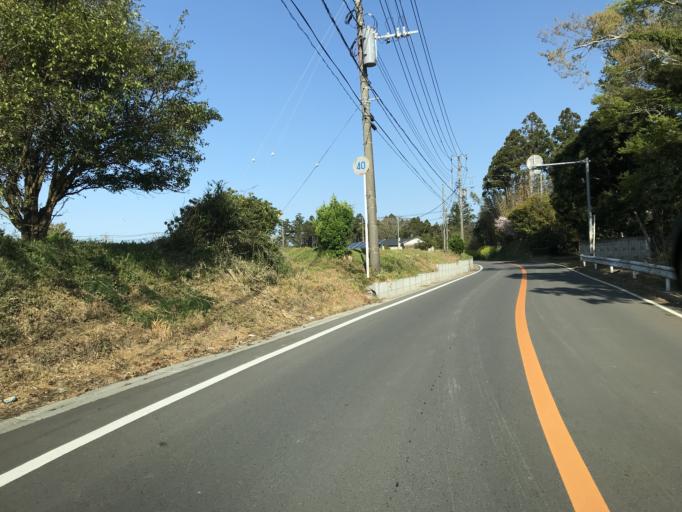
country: JP
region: Chiba
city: Omigawa
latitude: 35.8420
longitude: 140.5615
